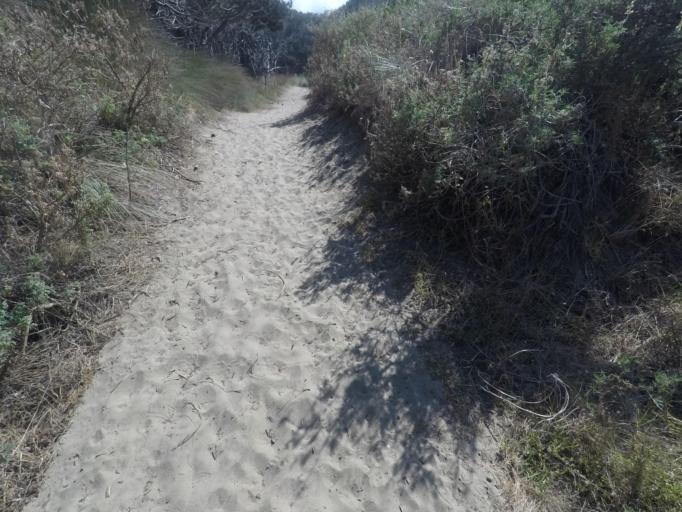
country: NZ
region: Auckland
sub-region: Auckland
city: Parakai
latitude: -36.6062
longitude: 174.2708
